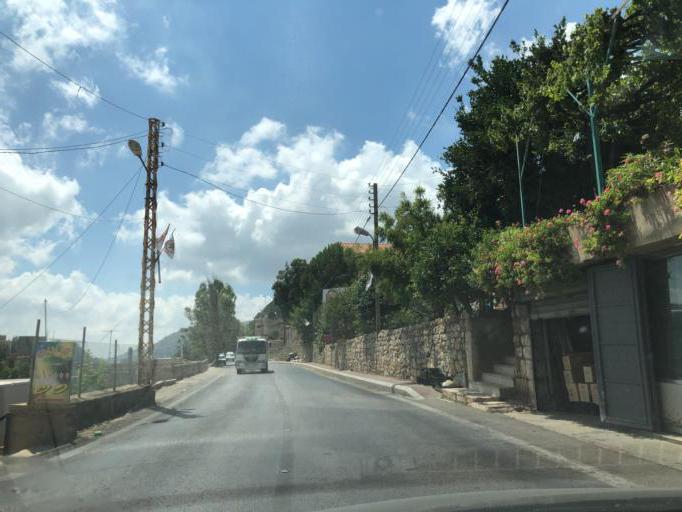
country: LB
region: Mont-Liban
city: Beit ed Dine
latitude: 33.7004
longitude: 35.5983
